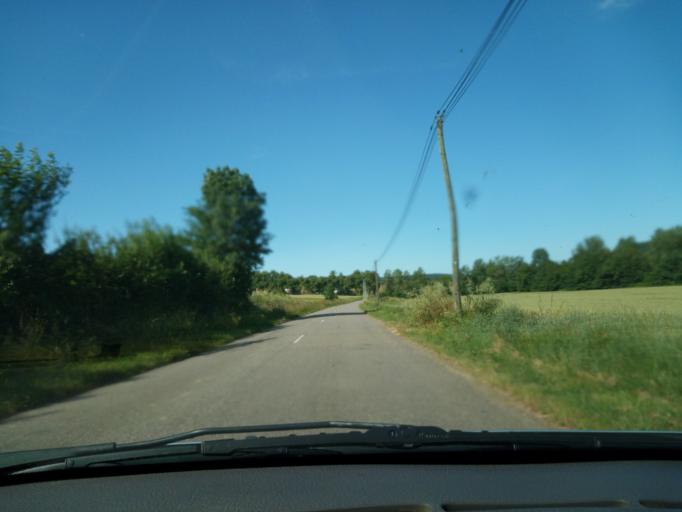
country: FR
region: Midi-Pyrenees
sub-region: Departement du Lot
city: Castelnau-Montratier
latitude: 44.2482
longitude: 1.3482
